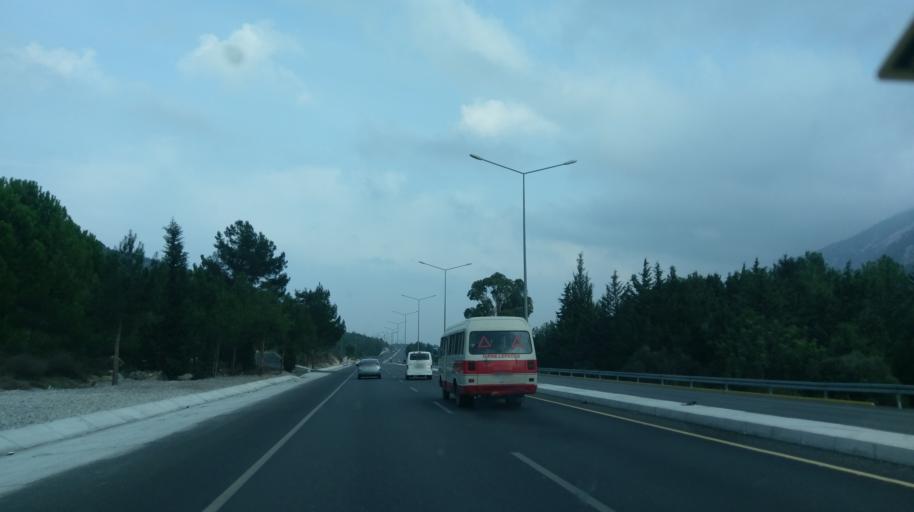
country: CY
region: Keryneia
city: Kyrenia
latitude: 35.3051
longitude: 33.2987
